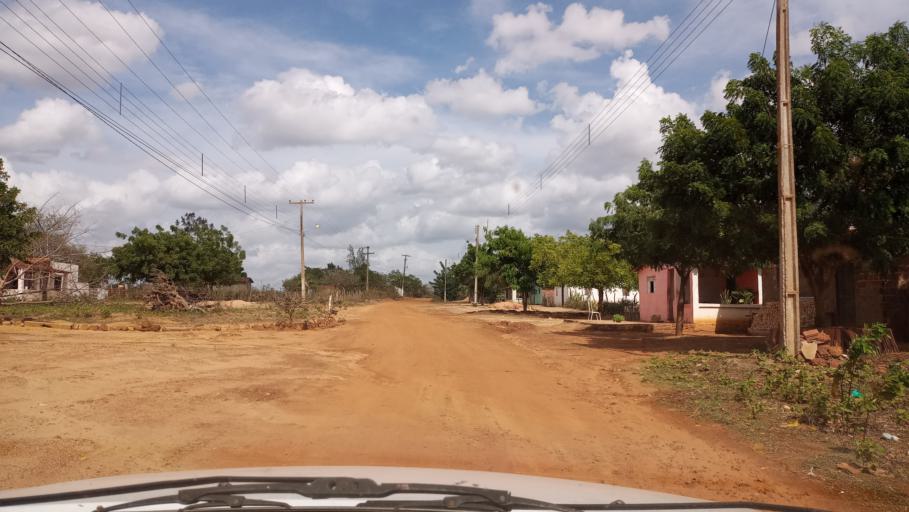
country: BR
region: Rio Grande do Norte
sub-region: Joao Camara
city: Joao Camara
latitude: -5.4698
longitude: -35.8295
